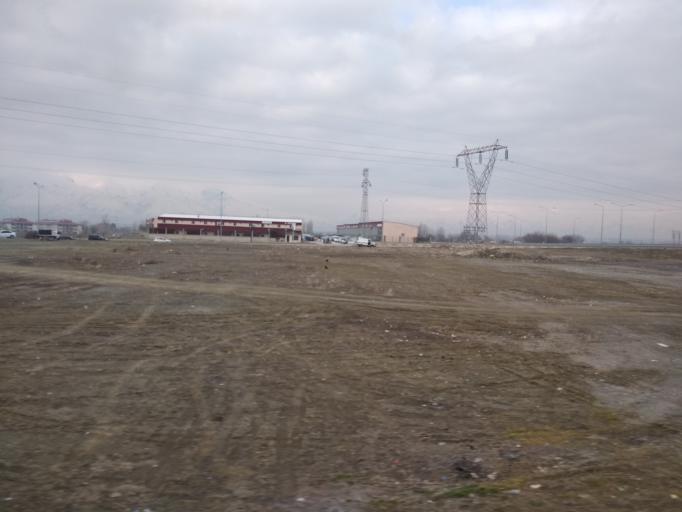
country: TR
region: Erzincan
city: Erzincan
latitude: 39.7319
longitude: 39.5335
